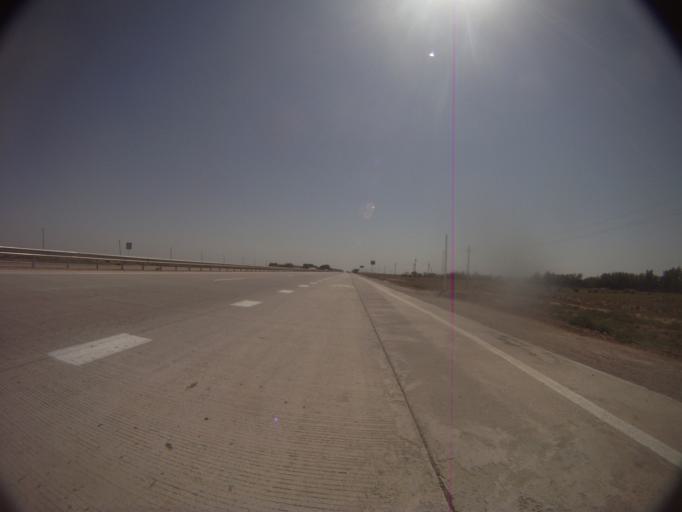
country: KZ
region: Ongtustik Qazaqstan
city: Bayaldyr
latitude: 43.0631
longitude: 68.6792
